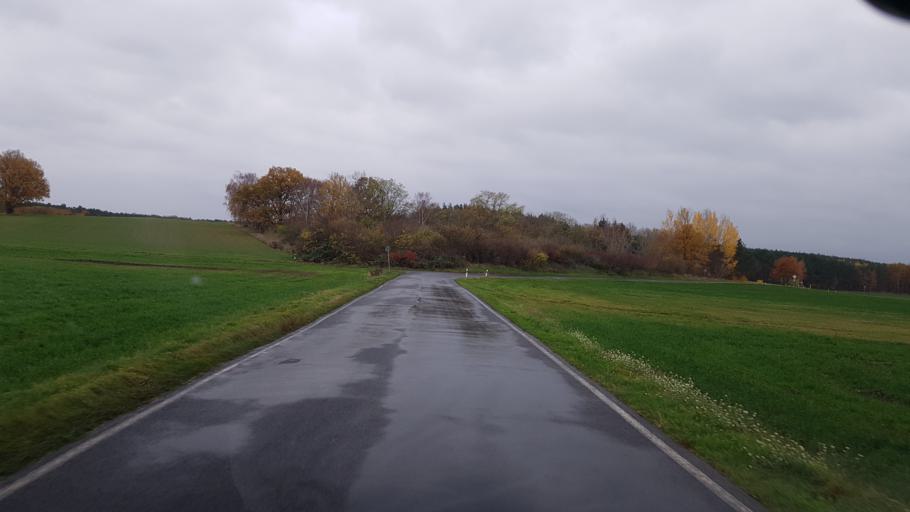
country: DE
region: Brandenburg
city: Ortrand
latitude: 51.3645
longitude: 13.7657
